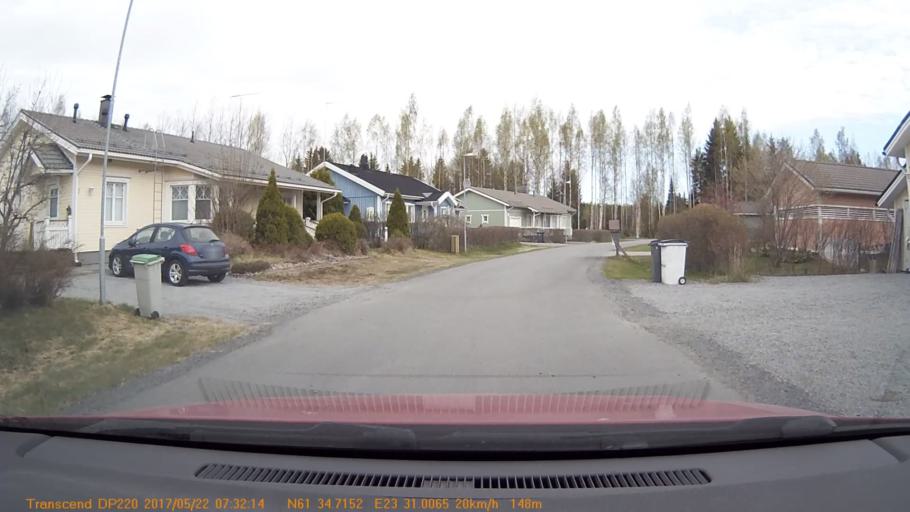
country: FI
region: Pirkanmaa
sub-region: Tampere
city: Yloejaervi
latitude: 61.5785
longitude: 23.5169
